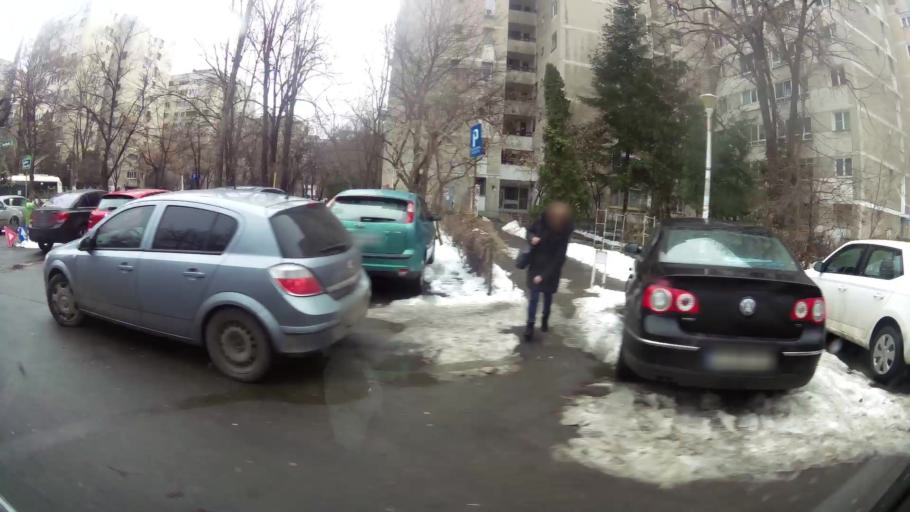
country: RO
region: Ilfov
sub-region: Comuna Chiajna
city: Rosu
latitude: 44.4212
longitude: 26.0475
